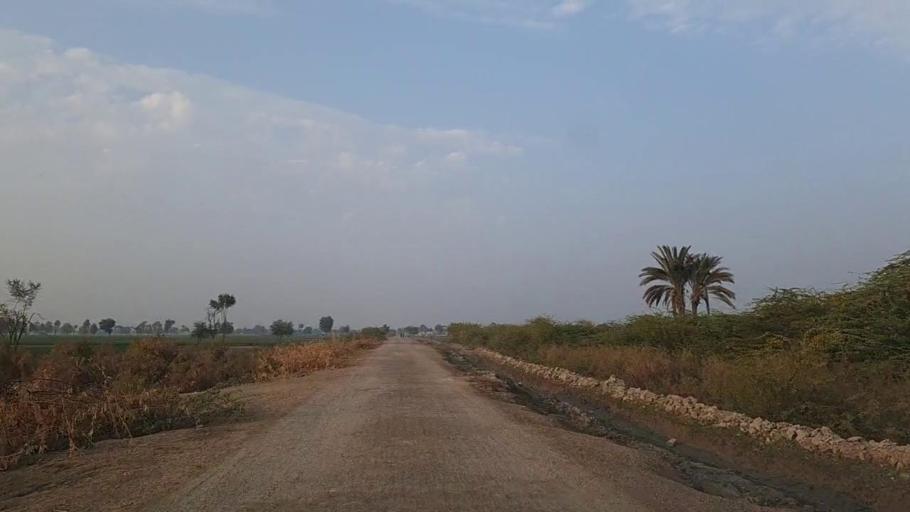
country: PK
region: Sindh
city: Jam Sahib
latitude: 26.3074
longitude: 68.6088
